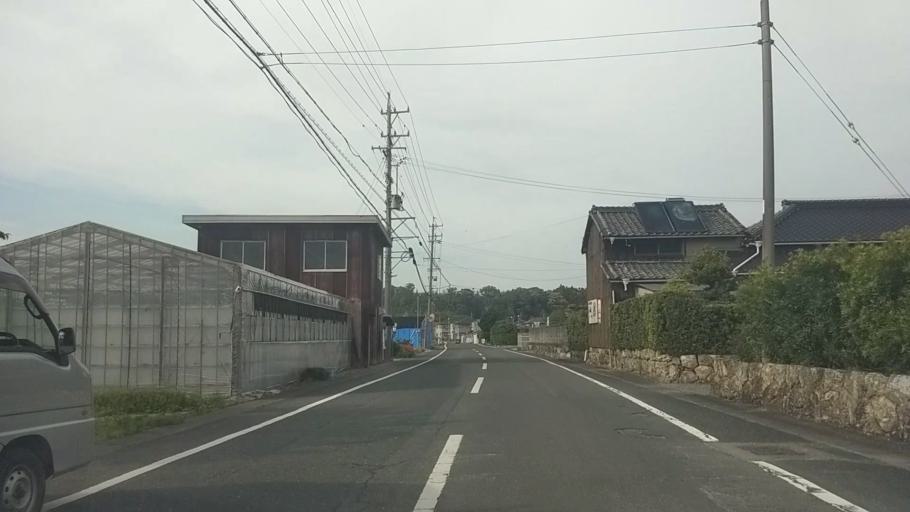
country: JP
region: Shizuoka
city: Kosai-shi
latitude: 34.7413
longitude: 137.6137
